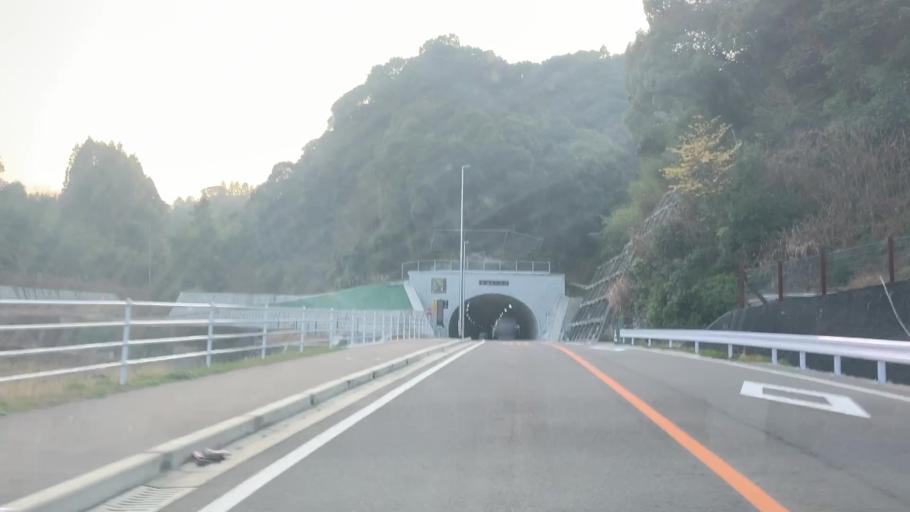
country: JP
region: Saga Prefecture
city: Takeocho-takeo
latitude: 33.2614
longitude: 130.0299
